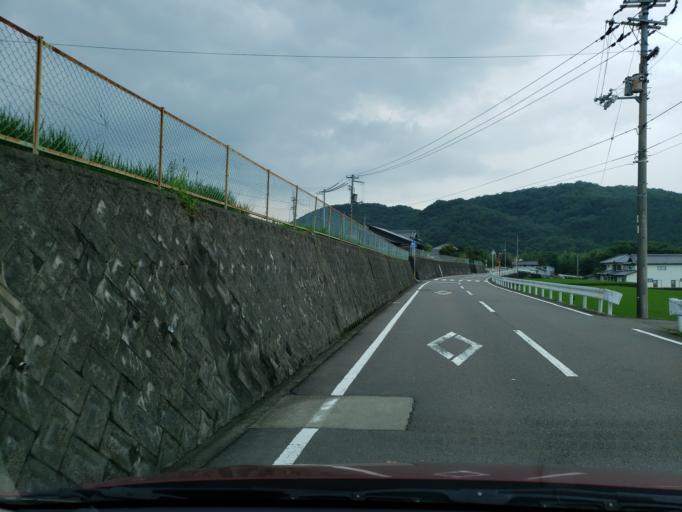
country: JP
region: Tokushima
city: Kamojimacho-jogejima
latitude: 34.1078
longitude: 134.2835
